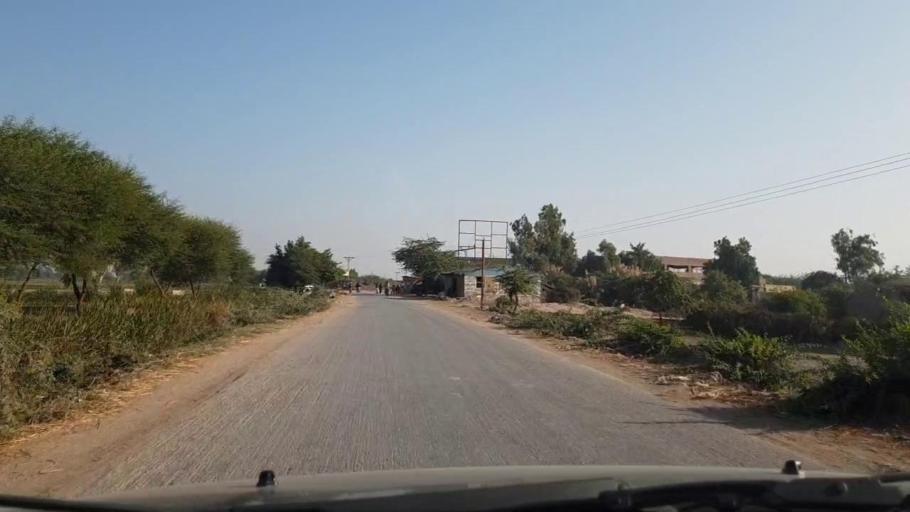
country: PK
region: Sindh
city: Tando Bago
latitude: 24.7934
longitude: 68.9741
